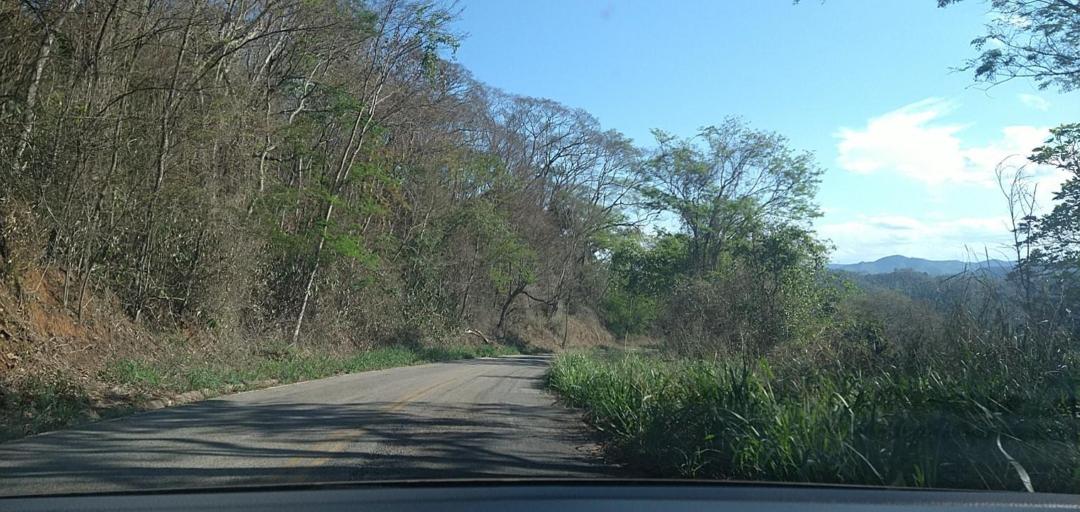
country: BR
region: Minas Gerais
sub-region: Ponte Nova
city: Ponte Nova
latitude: -20.2318
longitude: -42.9010
